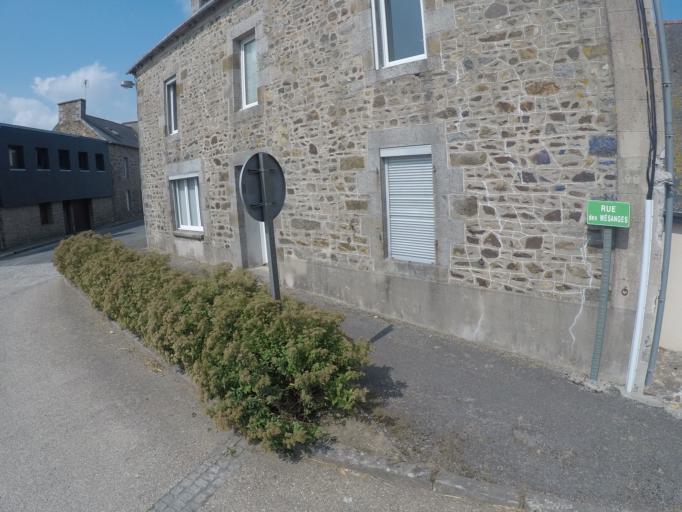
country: FR
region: Brittany
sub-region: Departement des Cotes-d'Armor
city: Tremuson
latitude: 48.5153
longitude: -2.8842
